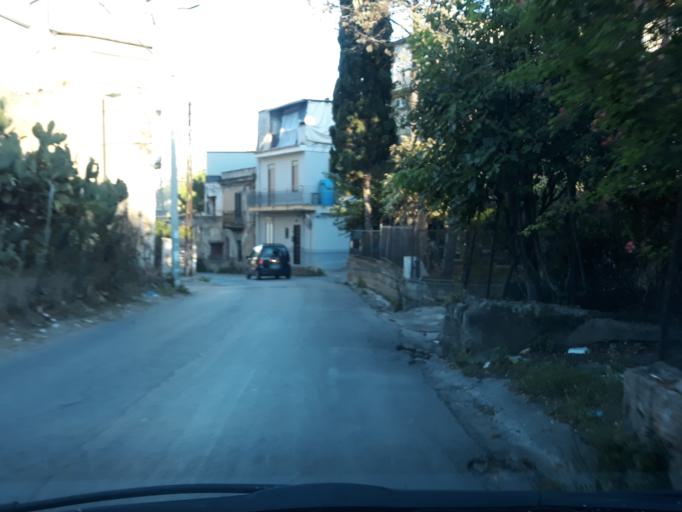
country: IT
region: Sicily
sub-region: Palermo
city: Monreale
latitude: 38.0746
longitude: 13.3074
